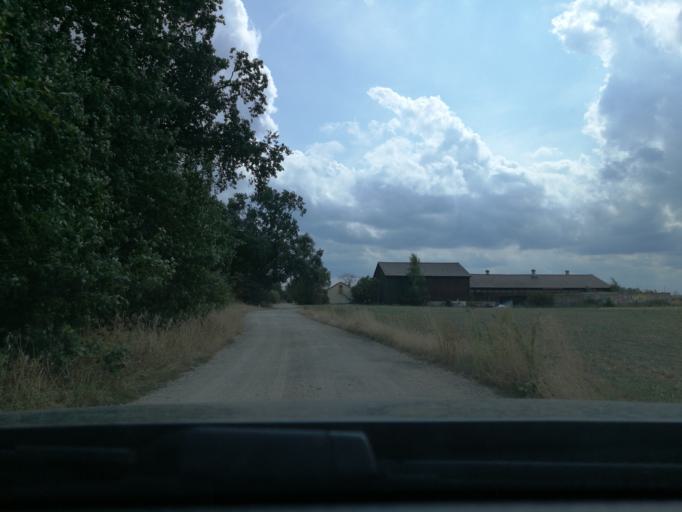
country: DE
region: Bavaria
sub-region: Regierungsbezirk Mittelfranken
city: Furth
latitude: 49.4948
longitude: 10.9514
